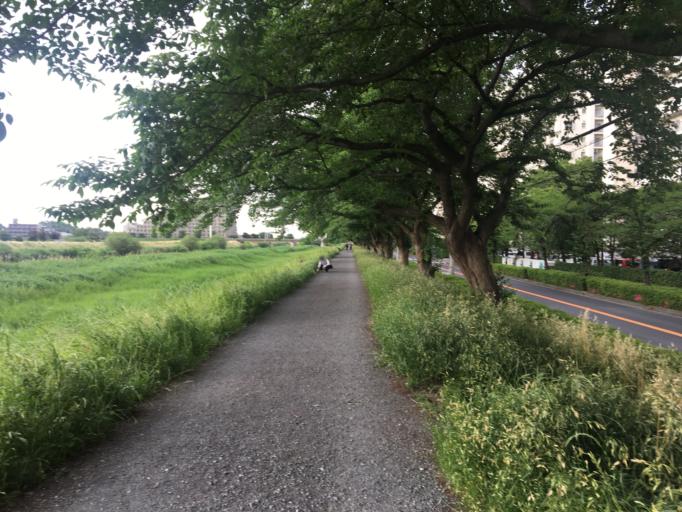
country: JP
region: Saitama
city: Shiki
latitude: 35.8287
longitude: 139.5574
